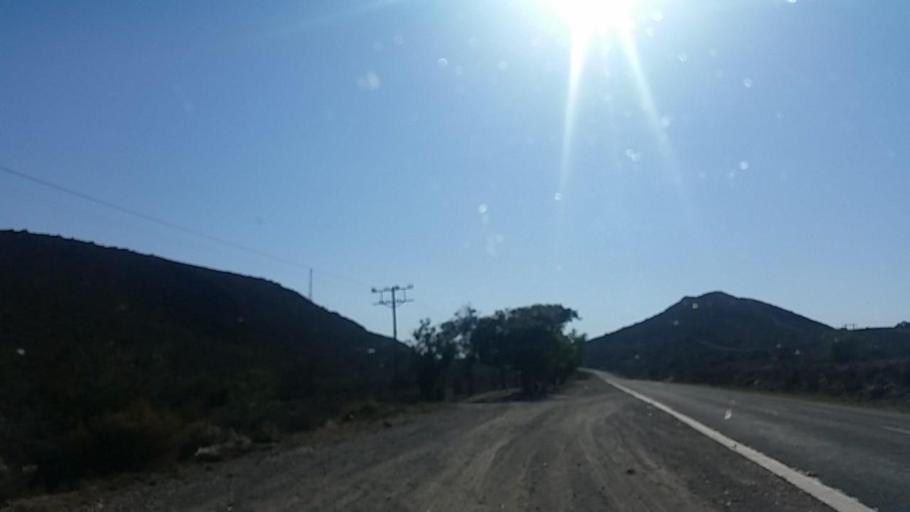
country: ZA
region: Eastern Cape
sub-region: Cacadu District Municipality
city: Willowmore
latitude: -33.3767
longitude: 23.4215
